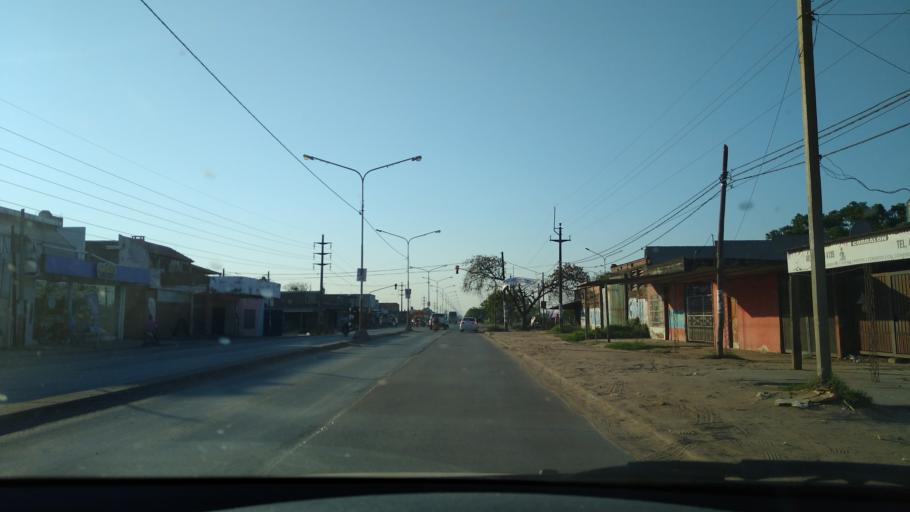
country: AR
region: Chaco
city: Barranqueras
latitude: -27.4898
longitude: -58.9571
